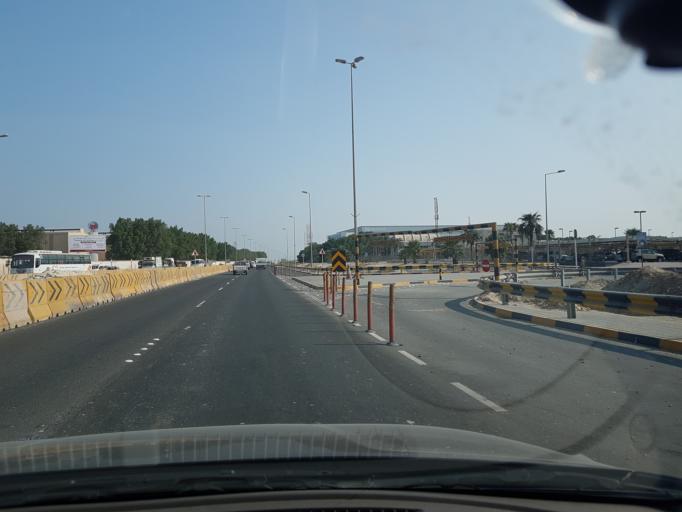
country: BH
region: Northern
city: Sitrah
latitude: 26.0857
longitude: 50.6118
